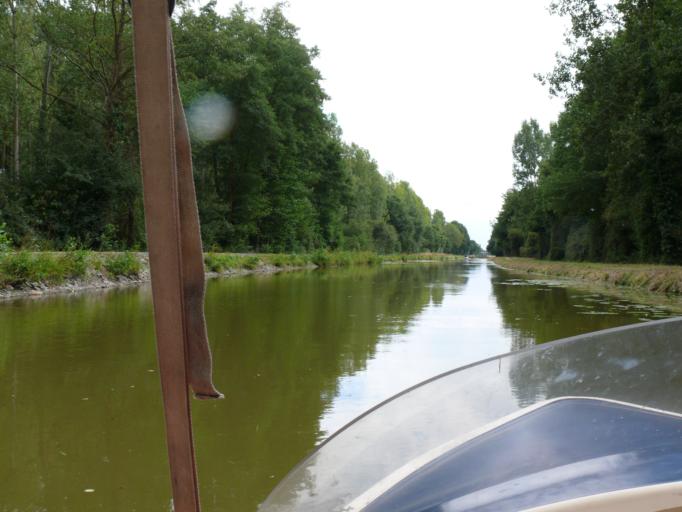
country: FR
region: Auvergne
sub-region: Departement de l'Allier
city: Vallon-en-Sully
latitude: 46.5229
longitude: 2.6160
